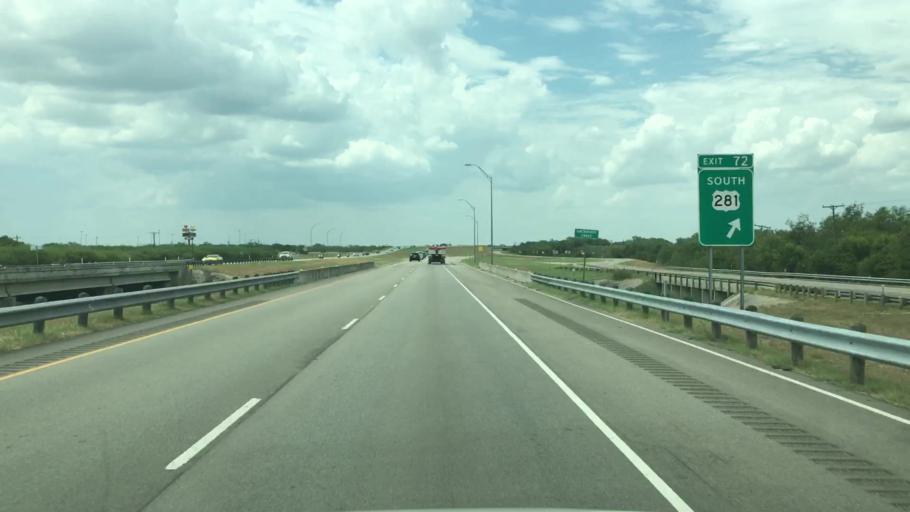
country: US
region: Texas
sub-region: Live Oak County
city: Three Rivers
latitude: 28.5182
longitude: -98.1777
